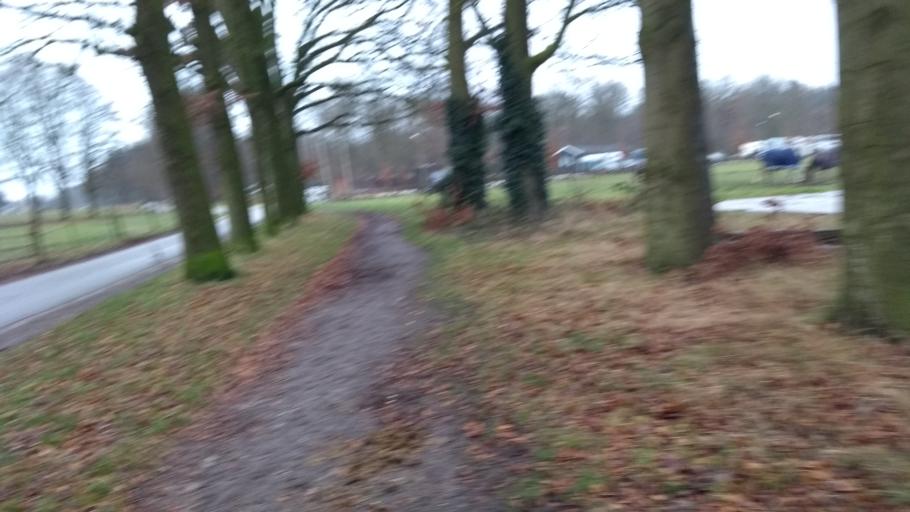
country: NL
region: Gelderland
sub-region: Gemeente Rheden
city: Dieren
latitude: 52.0697
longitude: 6.0799
